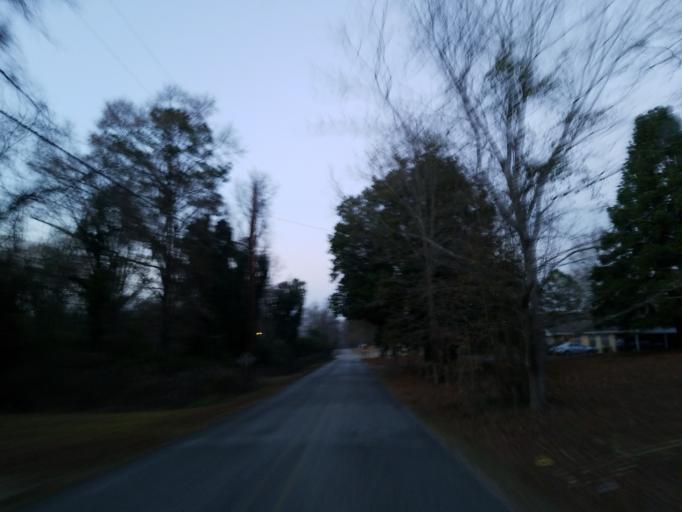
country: US
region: Alabama
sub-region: Sumter County
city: York
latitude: 32.4219
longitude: -88.4382
